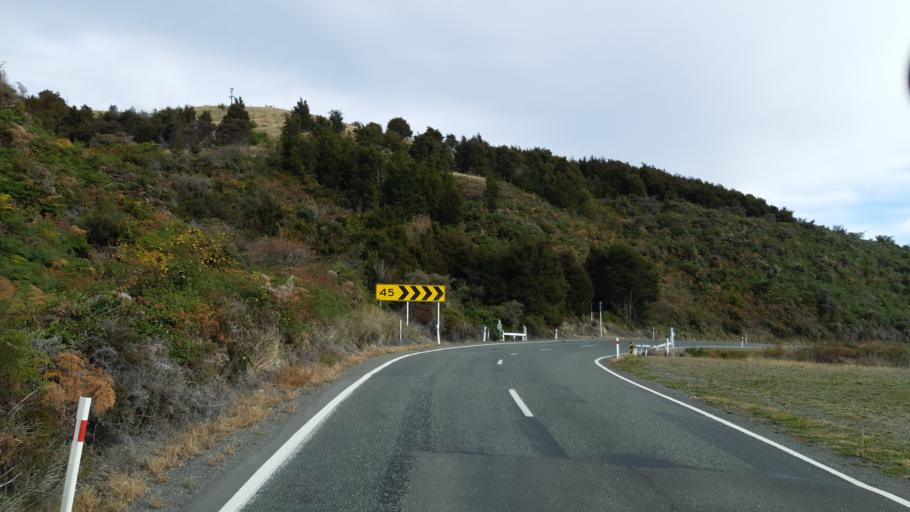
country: NZ
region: Tasman
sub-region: Tasman District
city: Wakefield
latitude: -41.6955
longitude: 173.1385
